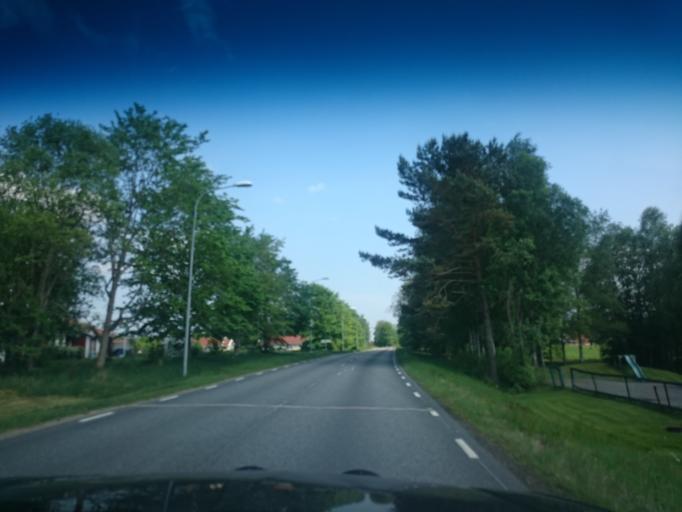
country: SE
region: Joenkoeping
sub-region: Vetlanda Kommun
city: Landsbro
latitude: 57.3823
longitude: 14.9686
